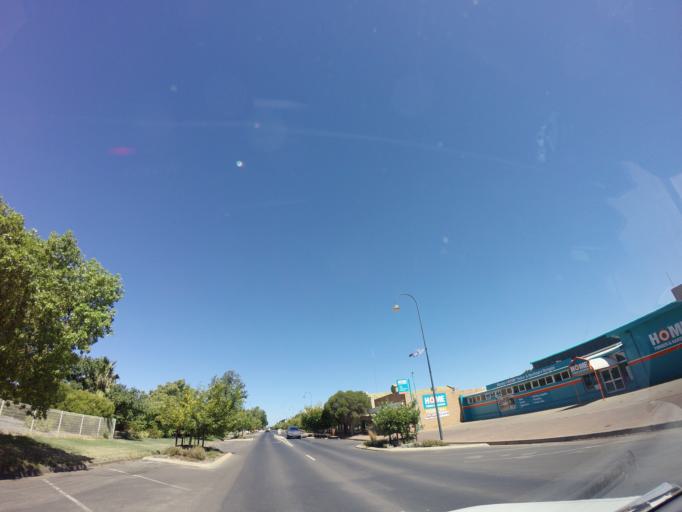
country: AU
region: New South Wales
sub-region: Bogan
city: Nyngan
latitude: -31.5617
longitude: 147.1937
